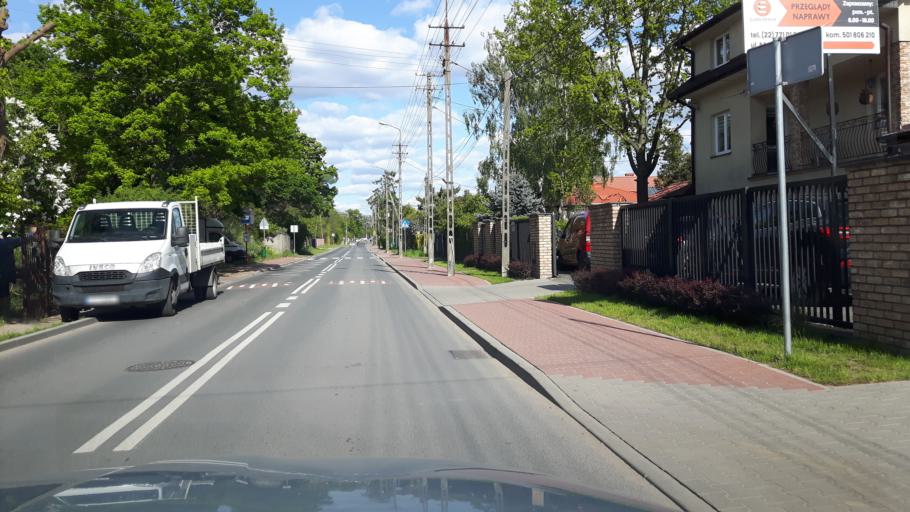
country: PL
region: Masovian Voivodeship
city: Zielonka
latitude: 52.3143
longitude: 21.1341
